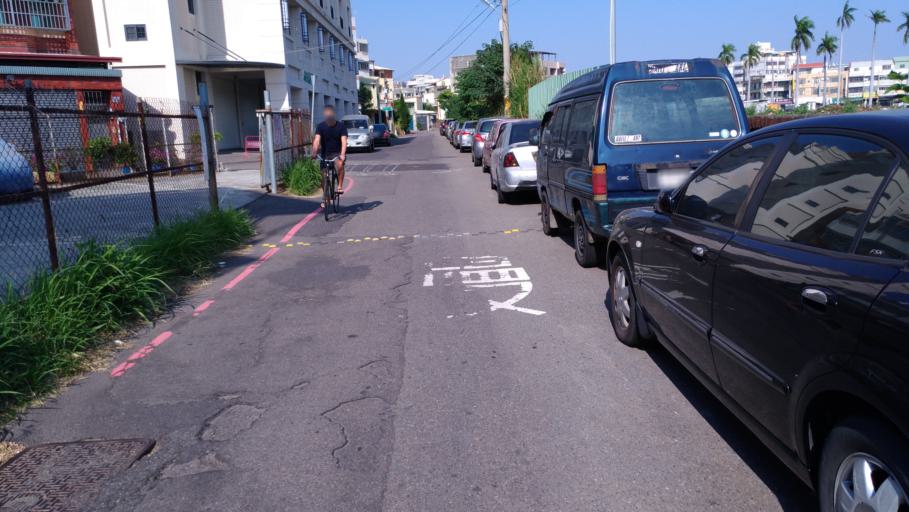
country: TW
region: Taiwan
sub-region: Changhua
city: Chang-hua
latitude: 24.0887
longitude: 120.5415
